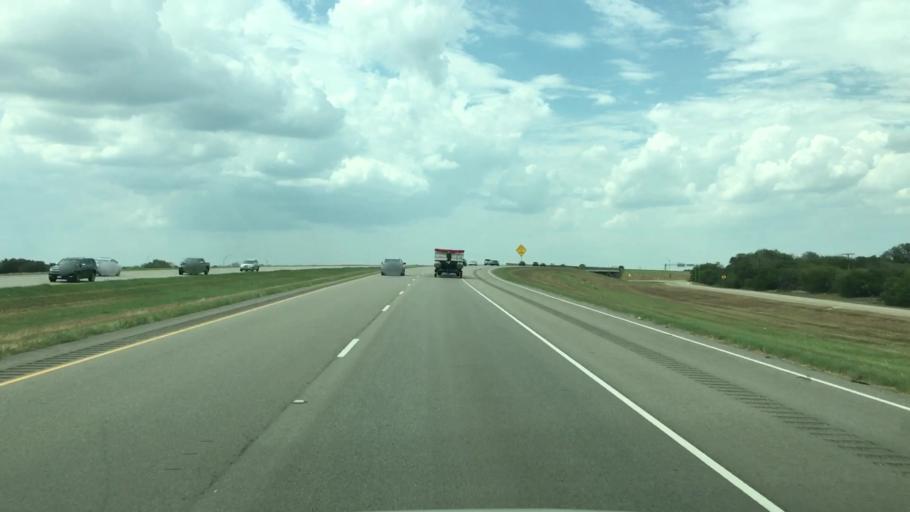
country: US
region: Texas
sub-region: Live Oak County
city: Three Rivers
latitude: 28.5226
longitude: -98.1832
